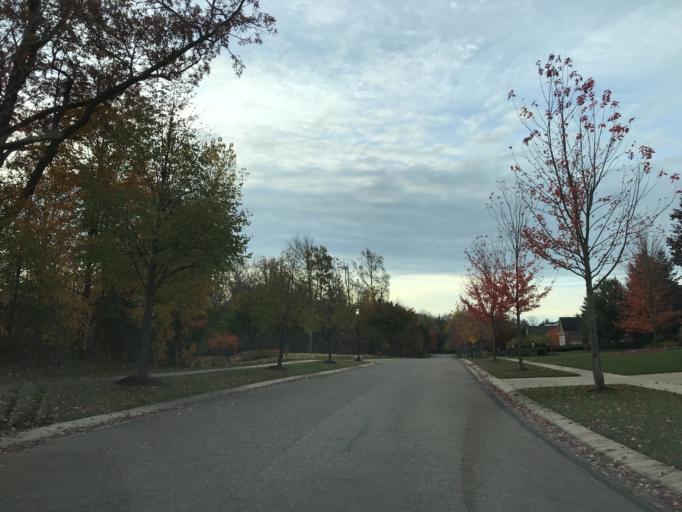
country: US
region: Michigan
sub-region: Oakland County
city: Wixom
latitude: 42.4764
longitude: -83.5395
